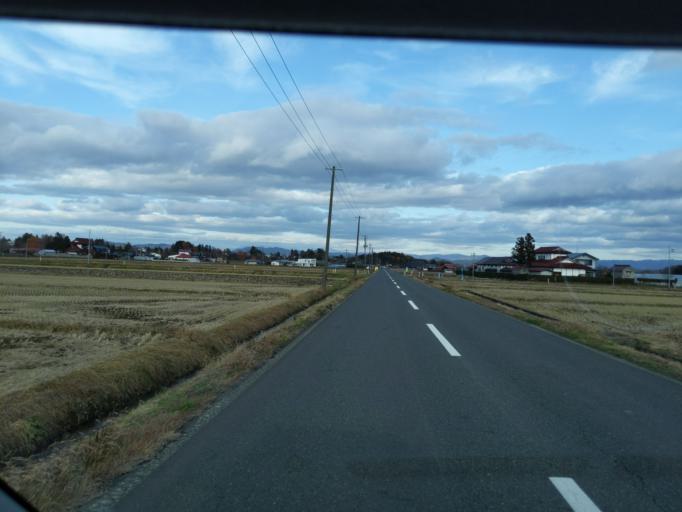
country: JP
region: Iwate
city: Mizusawa
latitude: 39.1779
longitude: 141.0983
